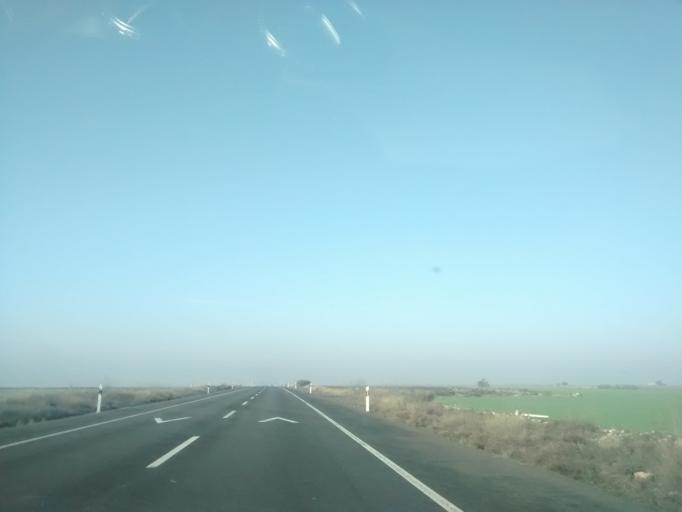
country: ES
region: Aragon
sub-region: Provincia de Huesca
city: Saidi / Zaidin
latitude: 41.5159
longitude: 0.2538
